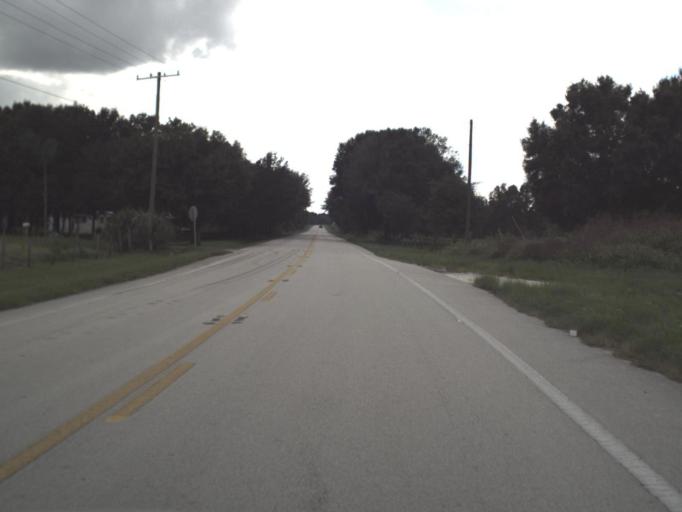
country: US
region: Florida
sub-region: Hardee County
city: Zolfo Springs
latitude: 27.5396
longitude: -81.7310
